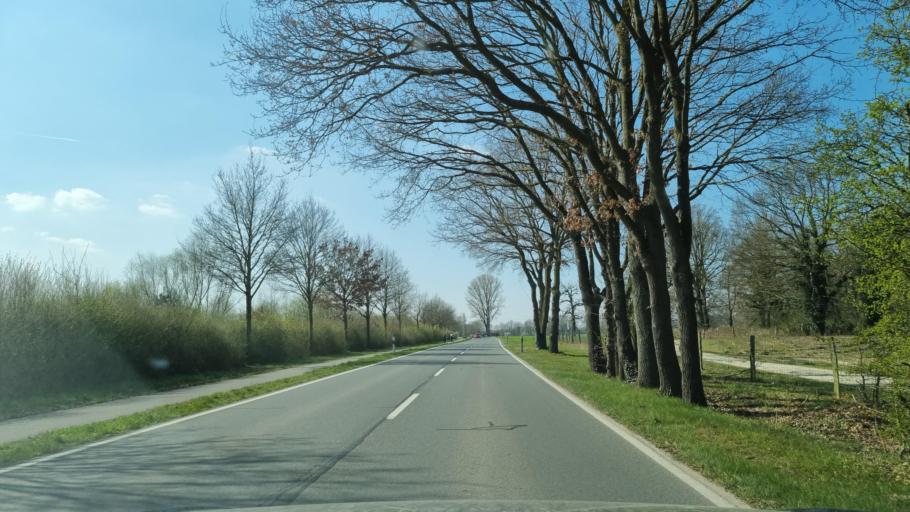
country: DE
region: North Rhine-Westphalia
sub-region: Regierungsbezirk Dusseldorf
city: Goch
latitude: 51.7026
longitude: 6.1119
